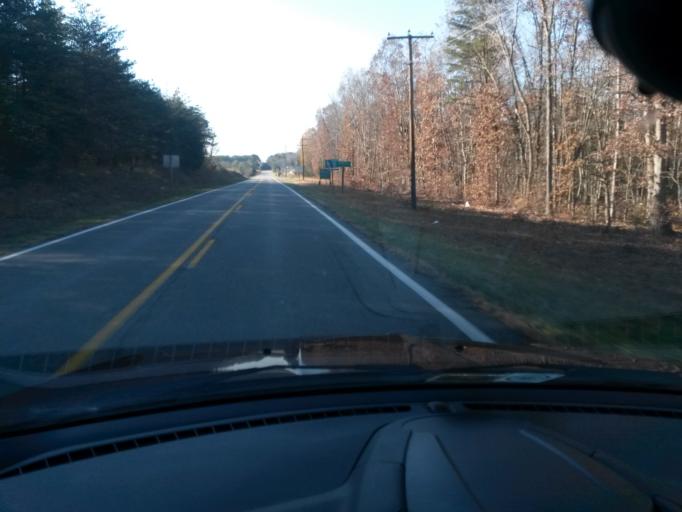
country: US
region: Virginia
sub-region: Charlotte County
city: Charlotte Court House
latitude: 37.2276
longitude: -78.6869
